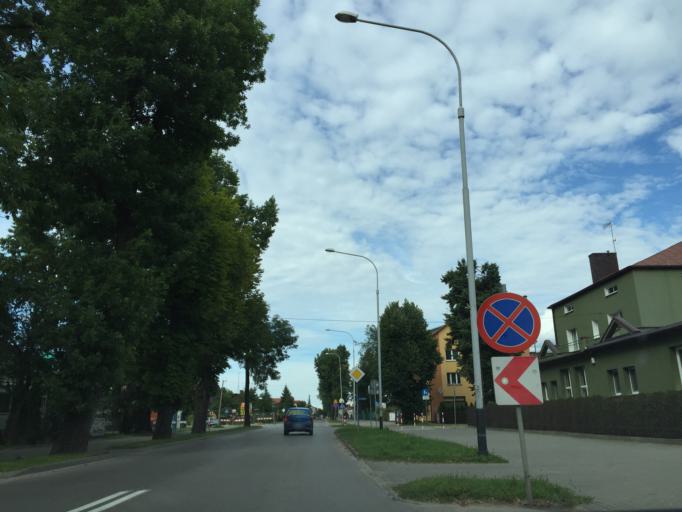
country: PL
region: Lublin Voivodeship
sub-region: Powiat lukowski
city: Lukow
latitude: 51.9346
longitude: 22.3788
